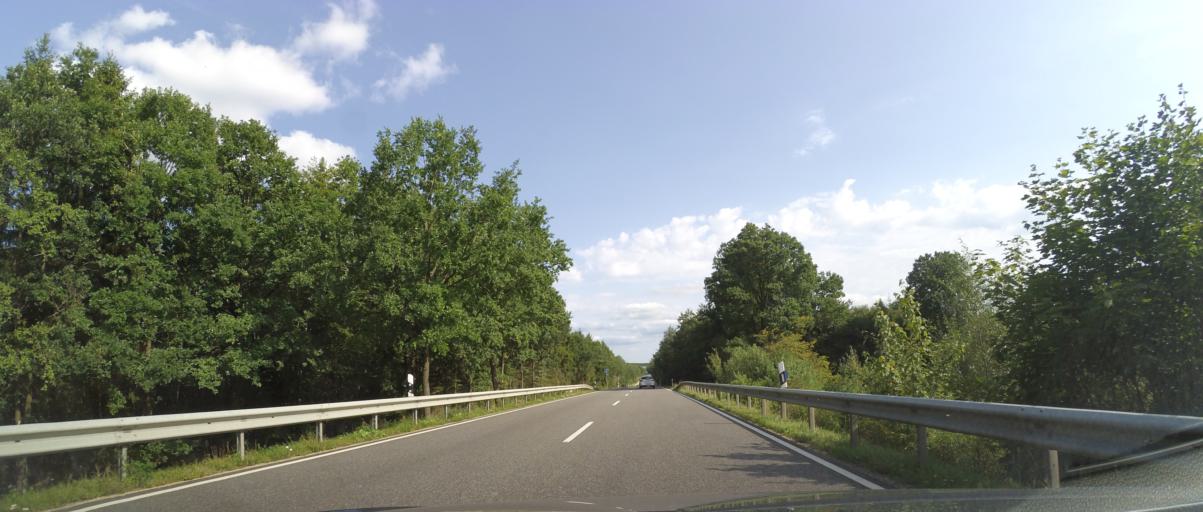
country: DE
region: Rheinland-Pfalz
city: Ohlenhard
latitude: 50.4360
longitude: 6.7327
